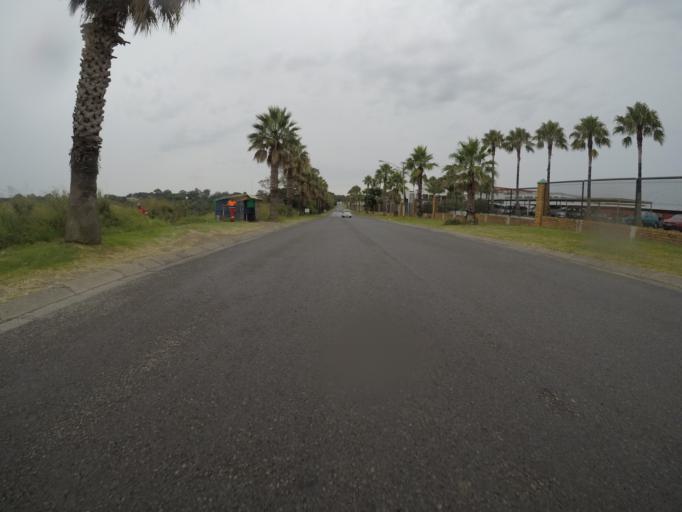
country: ZA
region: Eastern Cape
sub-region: Buffalo City Metropolitan Municipality
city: East London
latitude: -32.9734
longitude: 27.8181
